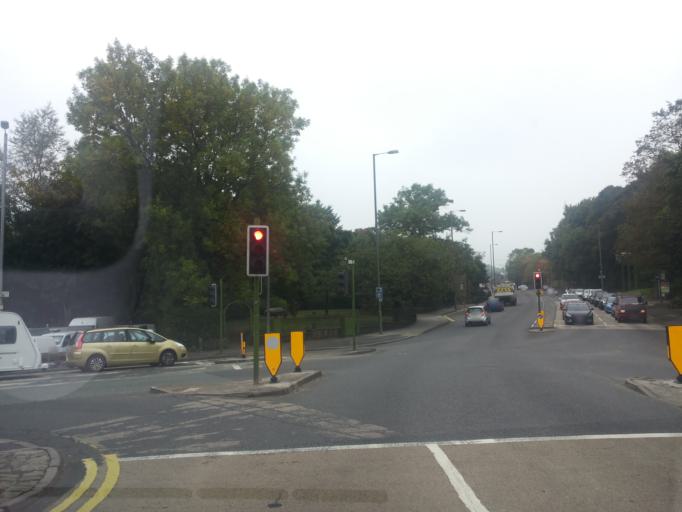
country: GB
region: England
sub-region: Borough of Tameside
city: Longdendale
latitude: 53.4611
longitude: -1.9959
